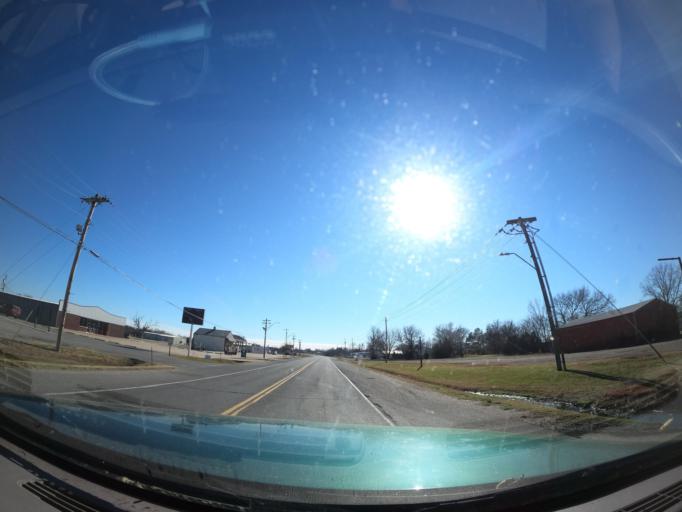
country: US
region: Oklahoma
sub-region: Muskogee County
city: Haskell
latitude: 35.8130
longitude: -95.6750
